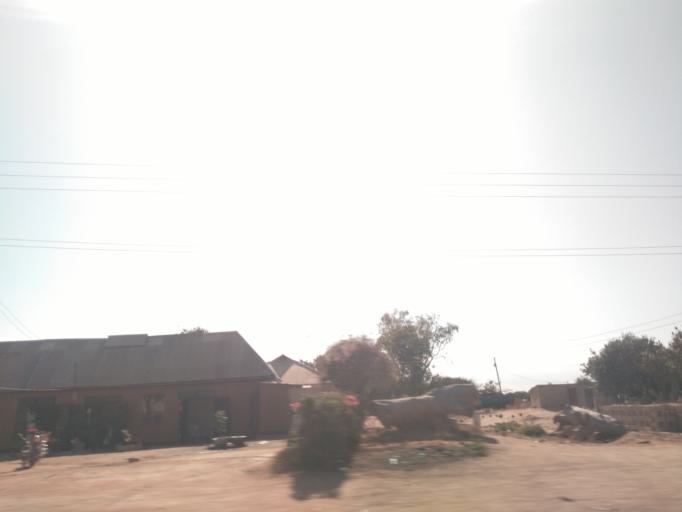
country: TZ
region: Dodoma
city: Dodoma
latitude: -6.1266
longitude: 35.7465
